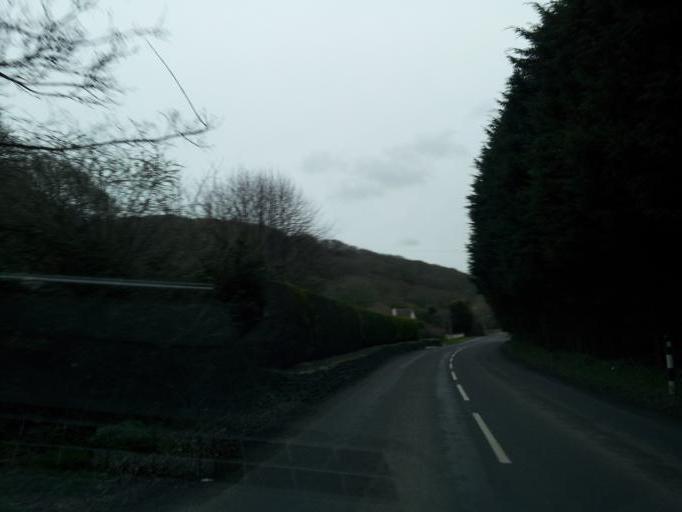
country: GB
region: England
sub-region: Cornwall
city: Camborne
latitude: 50.2588
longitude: -5.2722
